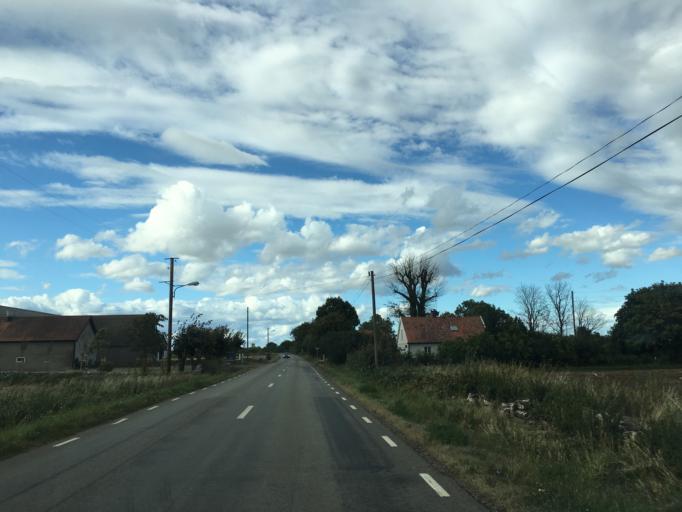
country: SE
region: Kalmar
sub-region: Morbylanga Kommun
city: Moerbylanga
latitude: 56.4198
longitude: 16.4353
